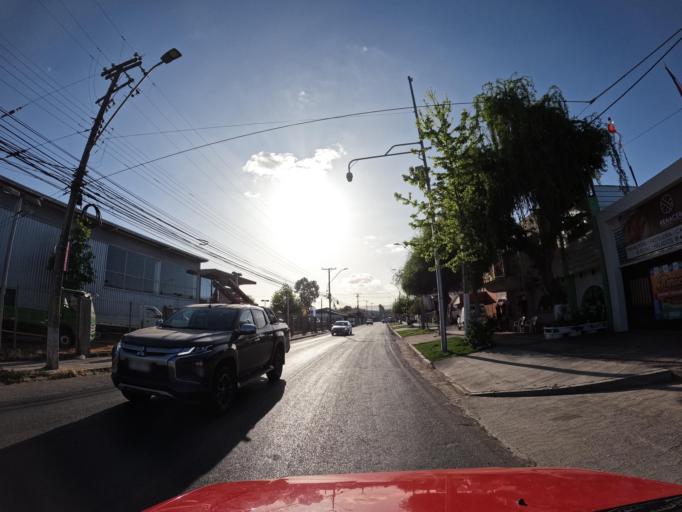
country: CL
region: O'Higgins
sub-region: Provincia de Colchagua
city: Santa Cruz
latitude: -34.6478
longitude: -71.3600
